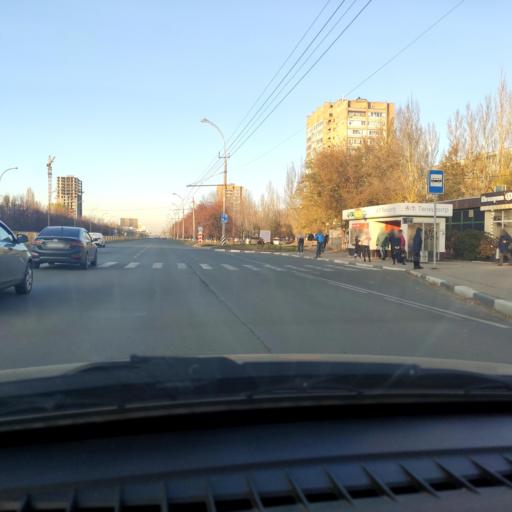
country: RU
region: Samara
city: Tol'yatti
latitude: 53.5216
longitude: 49.2957
